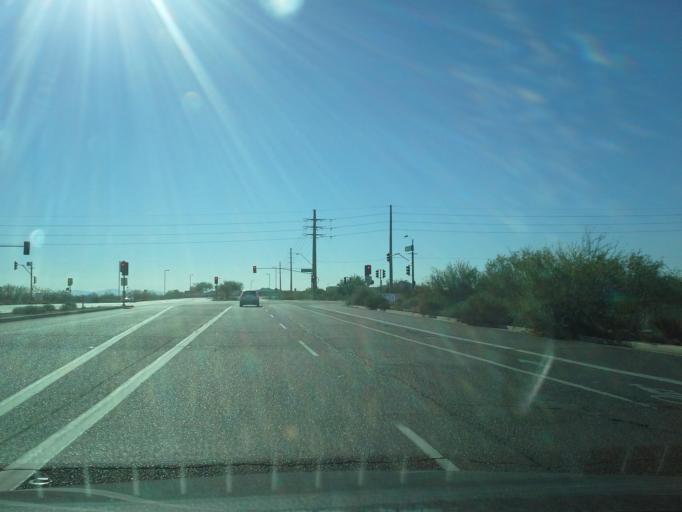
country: US
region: Arizona
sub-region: Maricopa County
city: Paradise Valley
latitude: 33.6637
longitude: -111.9589
